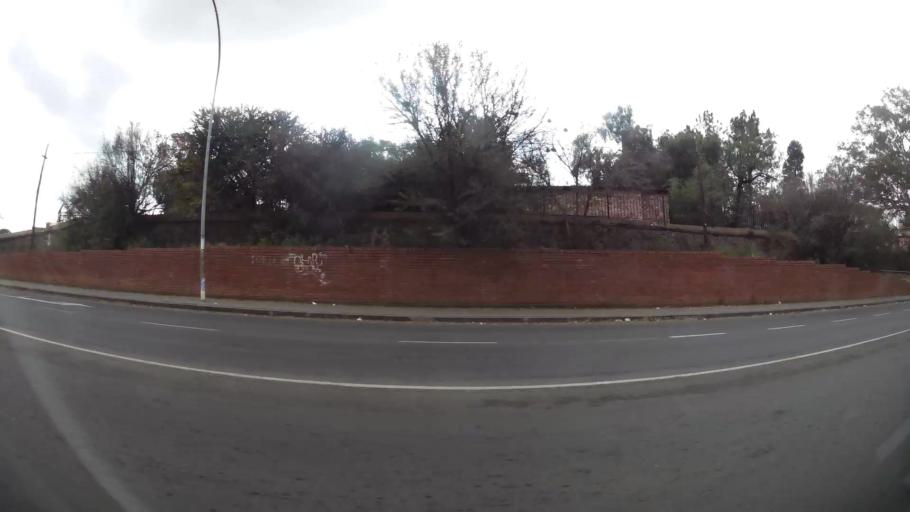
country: ZA
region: Orange Free State
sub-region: Mangaung Metropolitan Municipality
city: Bloemfontein
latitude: -29.1199
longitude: 26.2148
